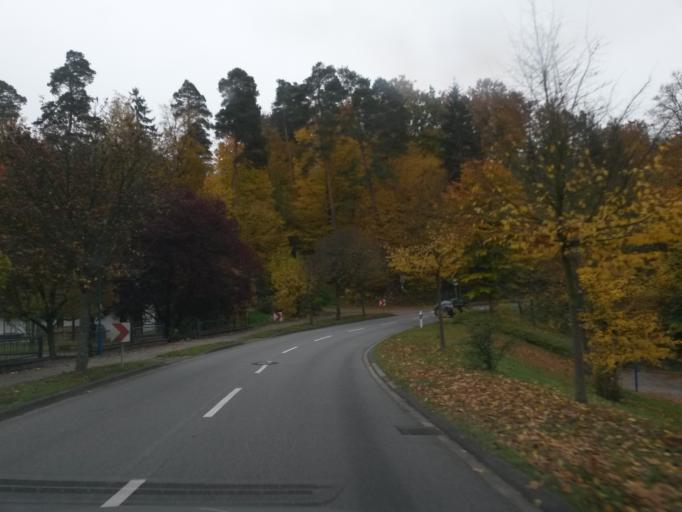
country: DE
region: Baden-Wuerttemberg
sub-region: Karlsruhe Region
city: Ettlingen
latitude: 48.9202
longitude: 8.4761
